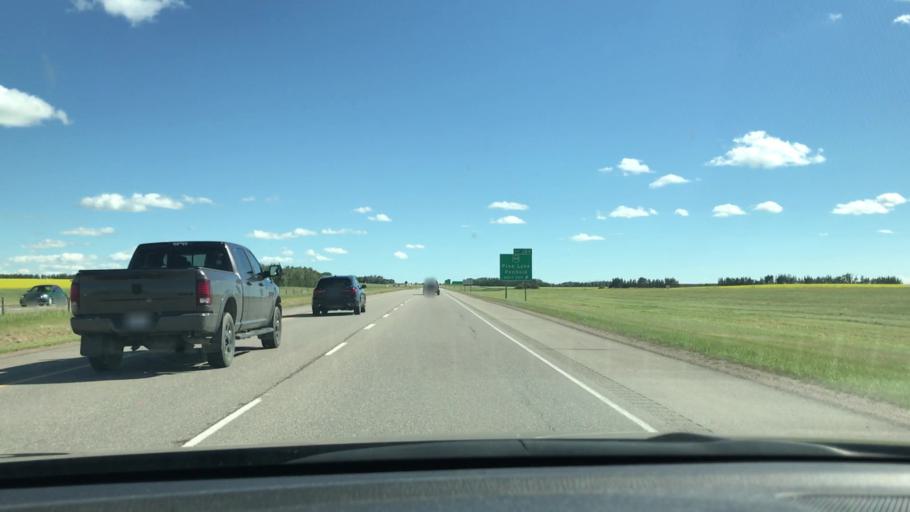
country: CA
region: Alberta
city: Penhold
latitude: 52.1638
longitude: -113.8140
